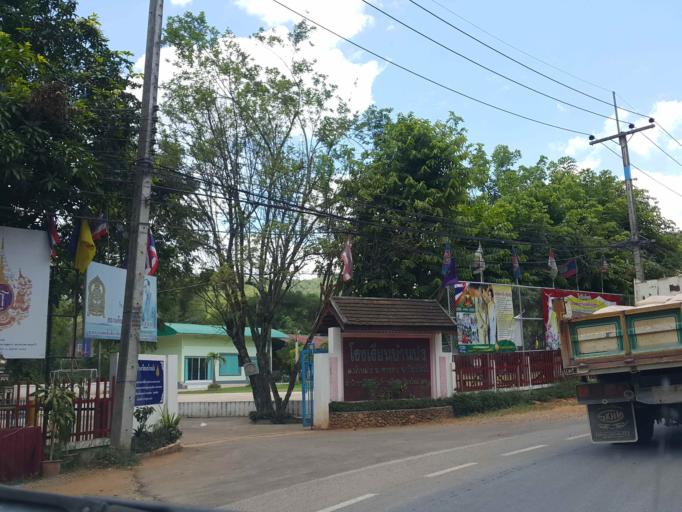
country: TH
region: Chiang Mai
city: Hang Dong
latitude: 18.7513
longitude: 98.8887
